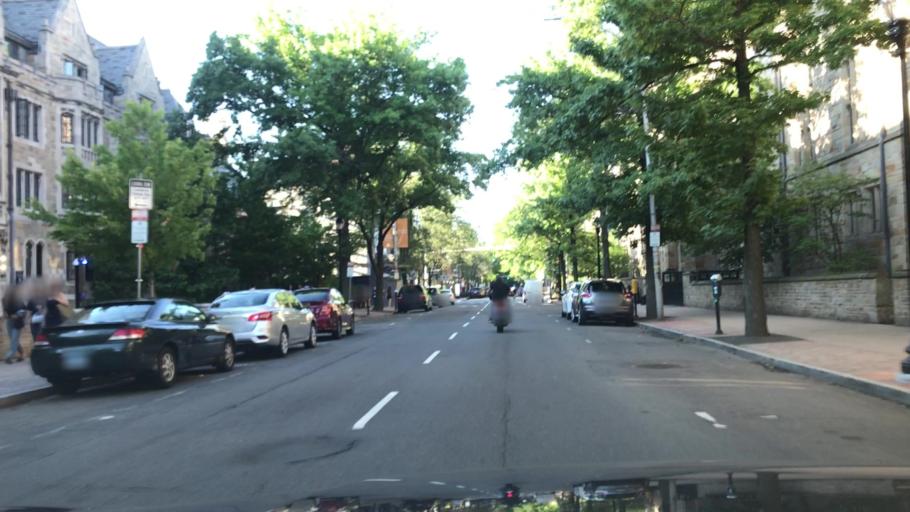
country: US
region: Connecticut
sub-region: New Haven County
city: New Haven
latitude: 41.3098
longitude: -72.9307
